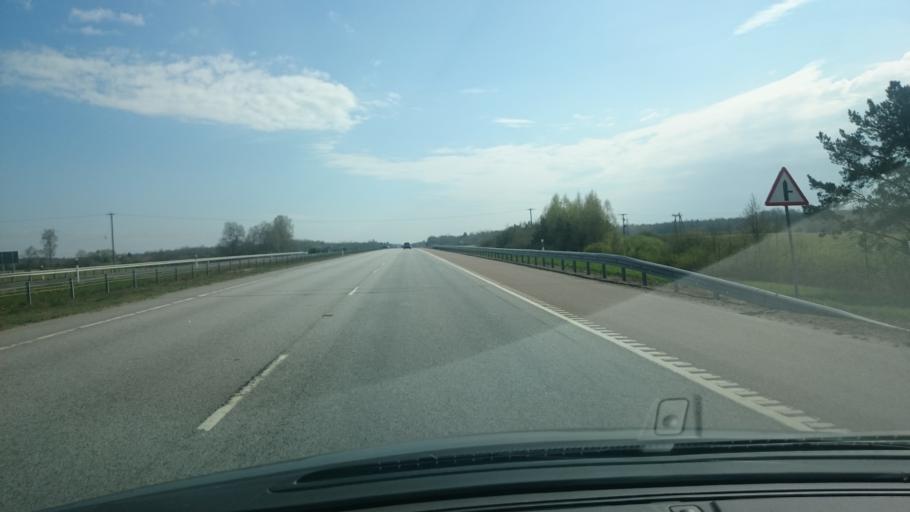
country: EE
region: Harju
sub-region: Anija vald
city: Kehra
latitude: 59.4410
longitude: 25.3026
